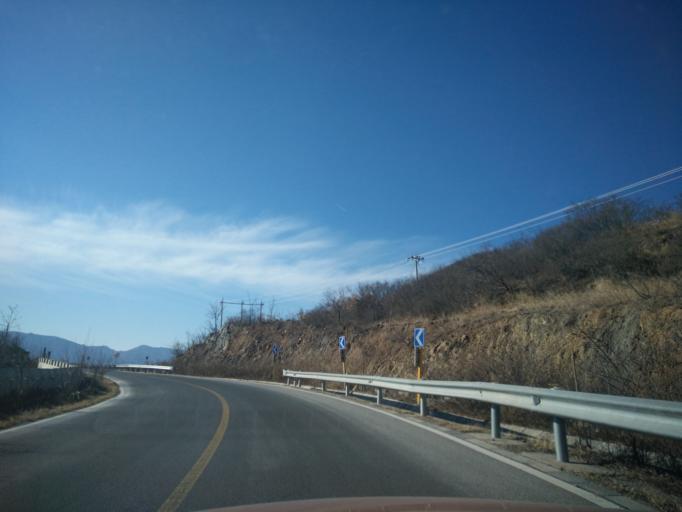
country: CN
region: Beijing
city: Zhaitang
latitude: 40.0219
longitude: 115.7066
